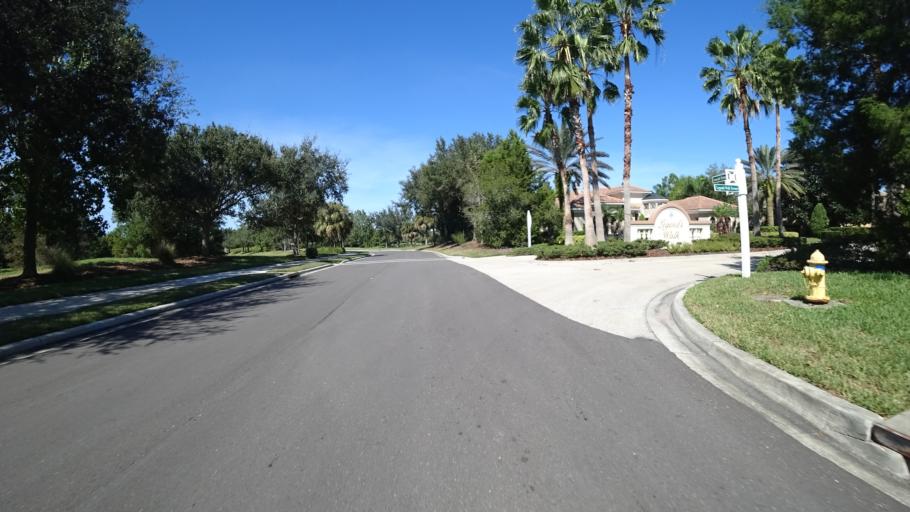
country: US
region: Florida
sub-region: Sarasota County
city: The Meadows
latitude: 27.4114
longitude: -82.4048
